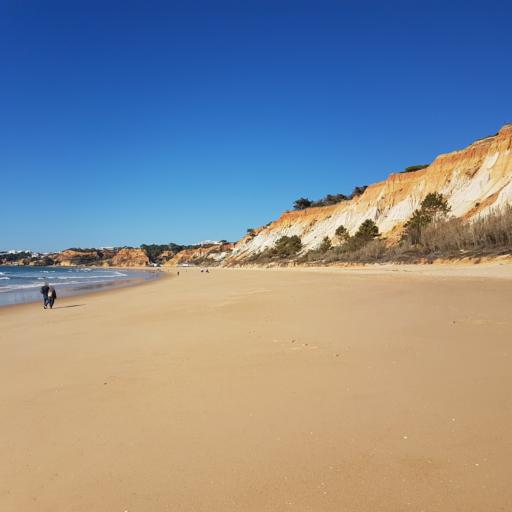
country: PT
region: Faro
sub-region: Loule
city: Boliqueime
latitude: 37.0877
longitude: -8.1731
